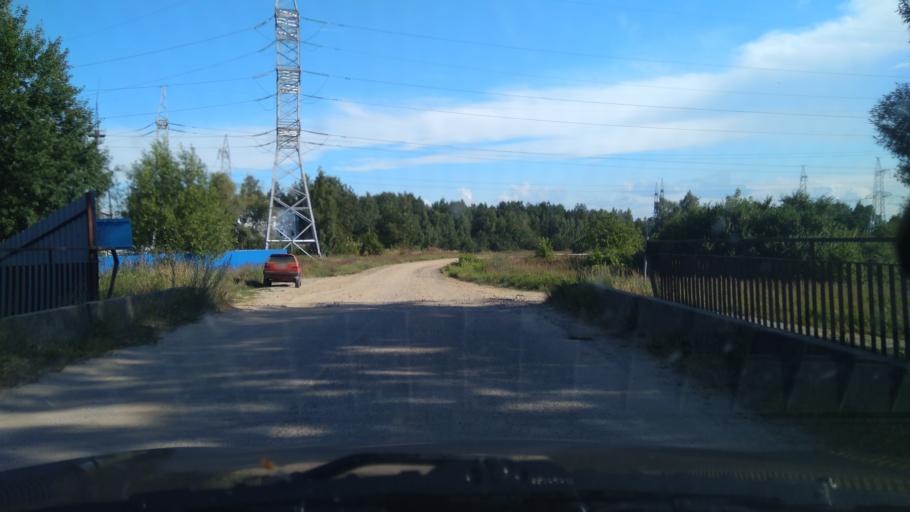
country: BY
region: Brest
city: Byelaazyorsk
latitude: 52.4554
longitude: 25.1871
